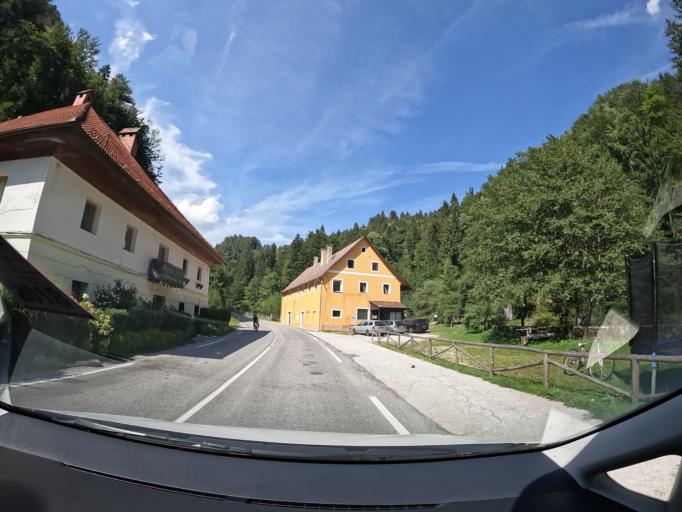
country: SI
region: Kranj
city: Golnik
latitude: 46.3821
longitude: 14.3850
